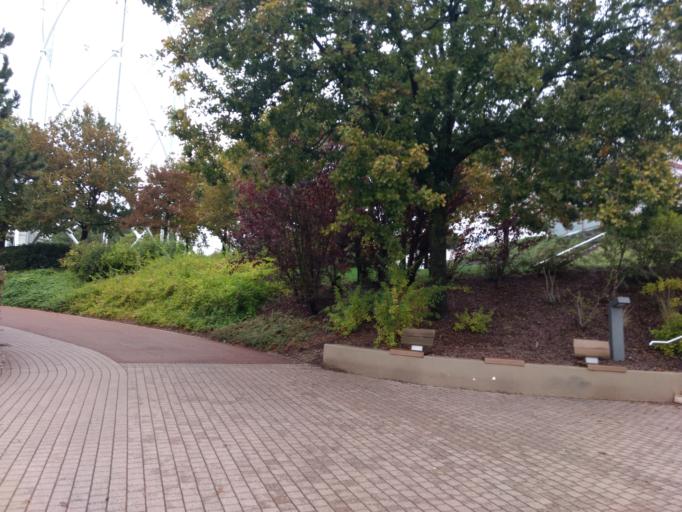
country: FR
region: Poitou-Charentes
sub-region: Departement de la Vienne
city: Jaunay-Clan
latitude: 46.6695
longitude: 0.3701
